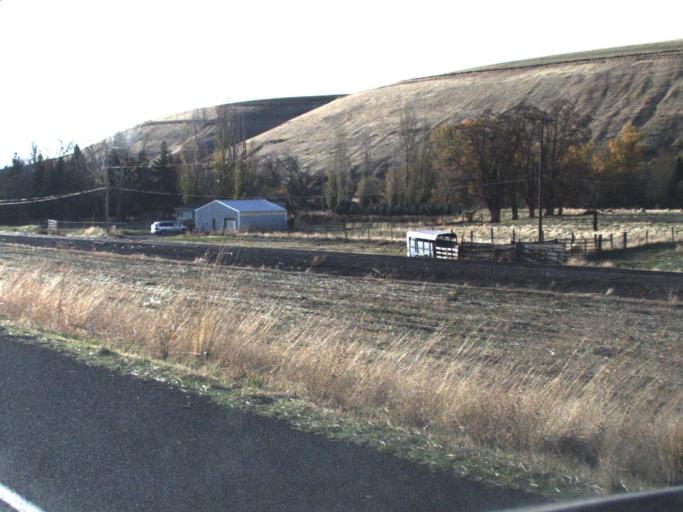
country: US
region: Washington
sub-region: Columbia County
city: Dayton
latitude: 46.3020
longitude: -118.0095
